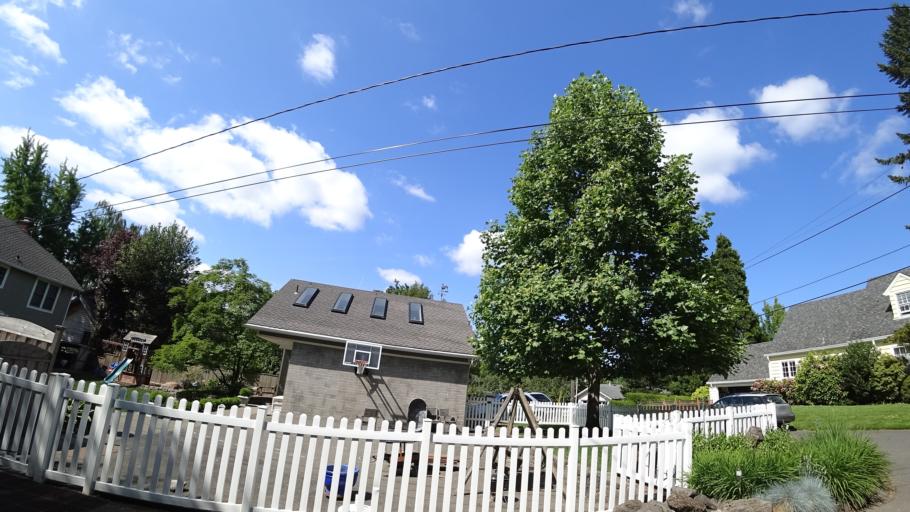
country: US
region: Oregon
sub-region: Washington County
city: Garden Home-Whitford
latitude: 45.4737
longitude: -122.7096
